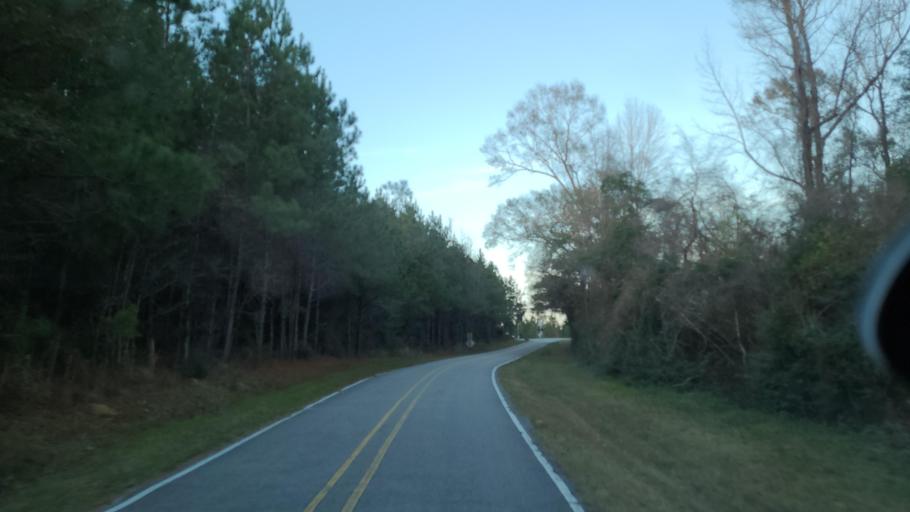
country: US
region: Mississippi
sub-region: Perry County
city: New Augusta
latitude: 31.1362
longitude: -89.2015
